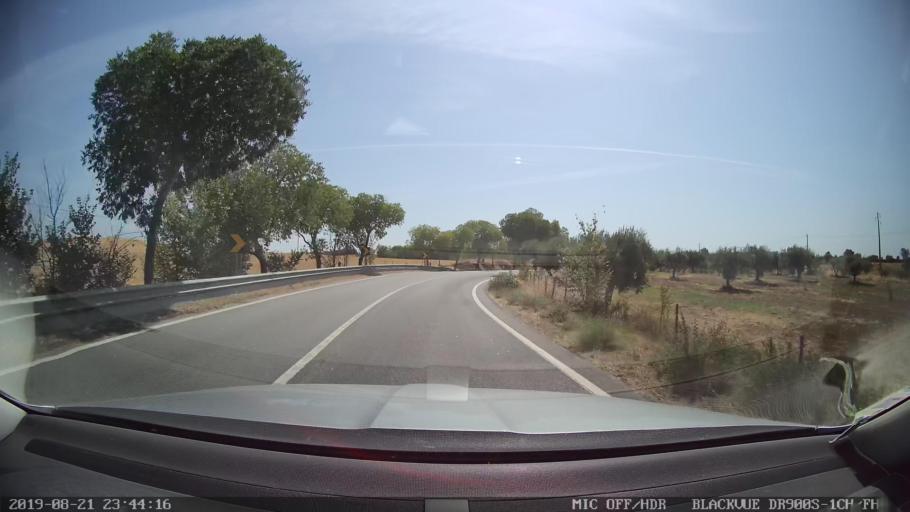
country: PT
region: Castelo Branco
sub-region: Idanha-A-Nova
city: Idanha-a-Nova
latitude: 39.8466
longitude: -7.2808
